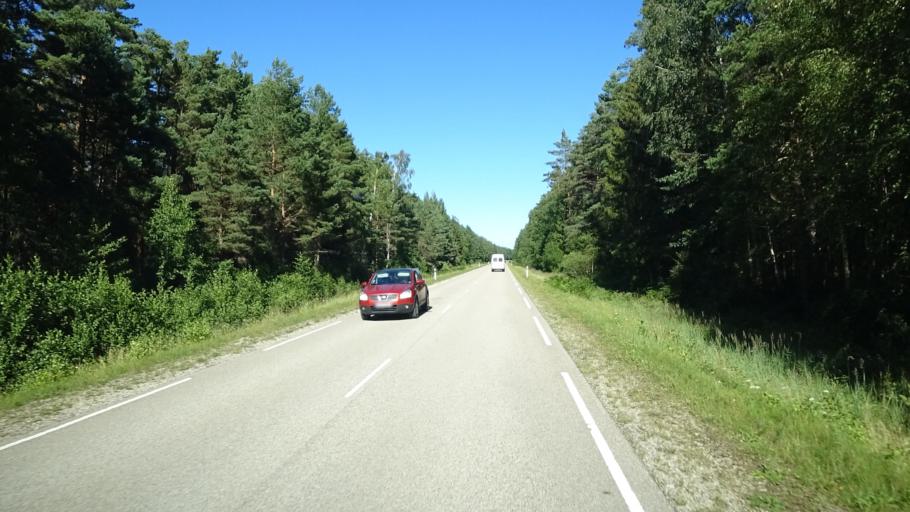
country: LV
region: Dundaga
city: Dundaga
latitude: 57.7402
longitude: 22.5386
